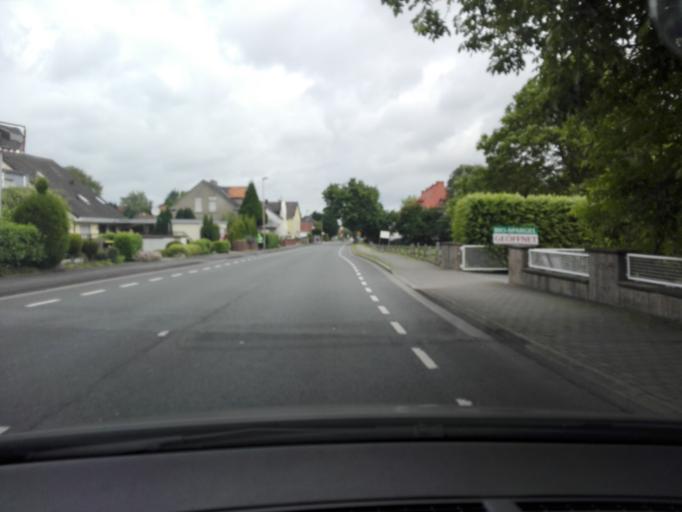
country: DE
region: North Rhine-Westphalia
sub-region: Regierungsbezirk Arnsberg
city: Unna
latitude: 51.5238
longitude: 7.6958
